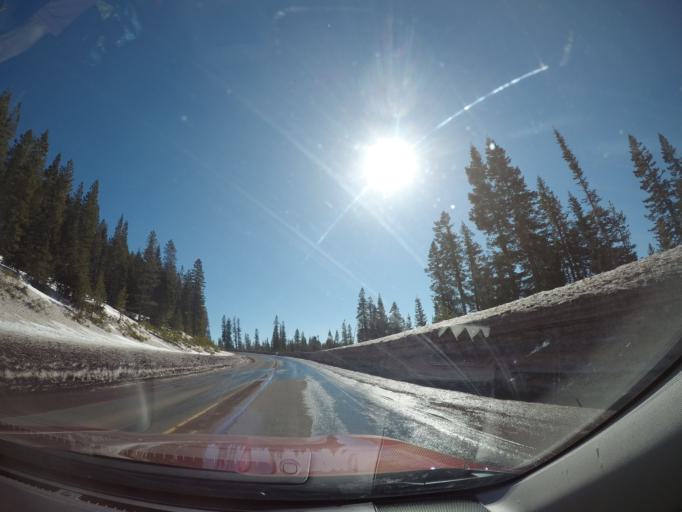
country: US
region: Oregon
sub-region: Deschutes County
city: Sunriver
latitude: 43.9813
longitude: -121.5897
